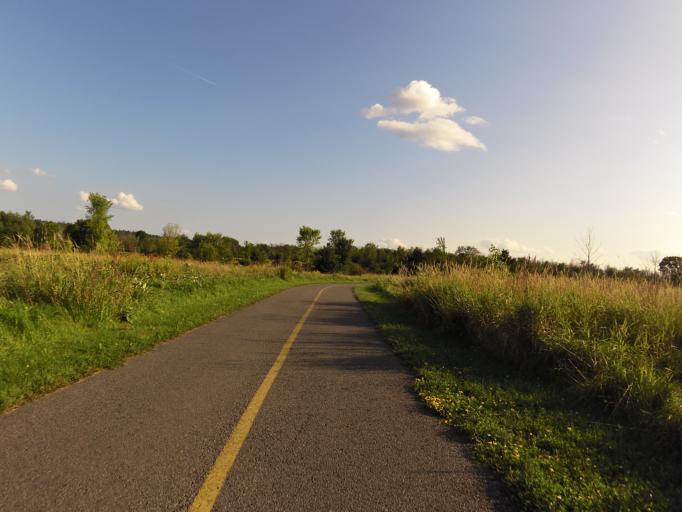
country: CA
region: Ontario
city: Bells Corners
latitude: 45.3427
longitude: -75.8802
